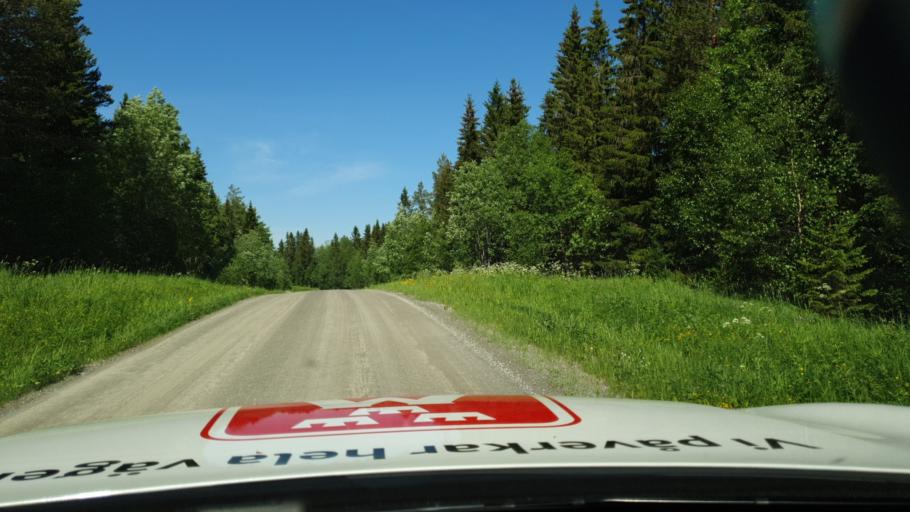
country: SE
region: Jaemtland
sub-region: Bergs Kommun
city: Hoverberg
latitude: 63.0187
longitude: 14.3790
